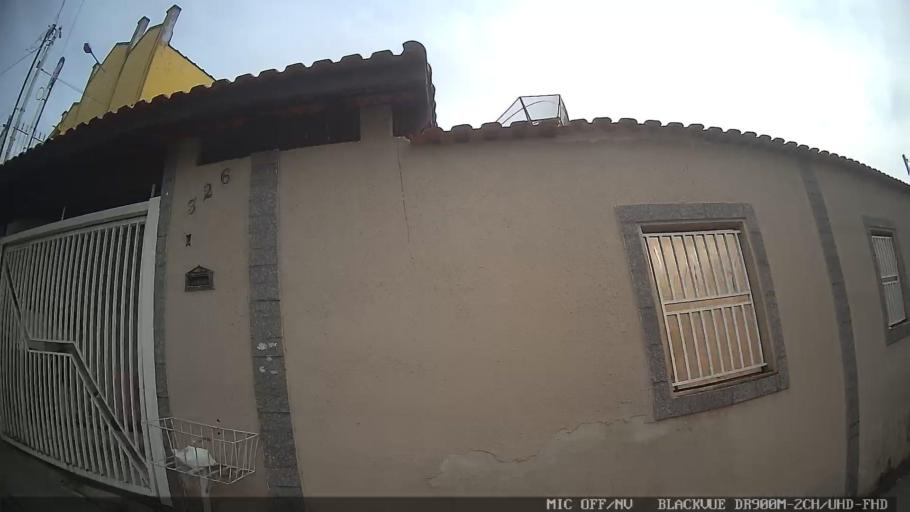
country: BR
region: Sao Paulo
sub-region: Poa
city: Poa
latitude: -23.5254
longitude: -46.3469
